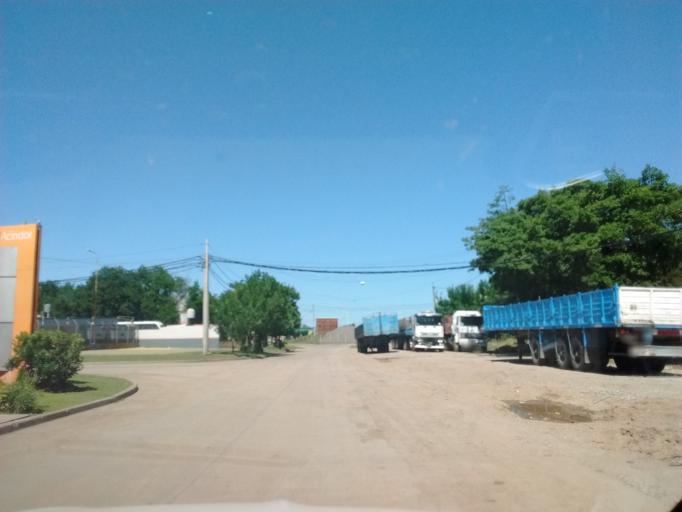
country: AR
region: Santa Fe
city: Perez
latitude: -32.9713
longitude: -60.7206
